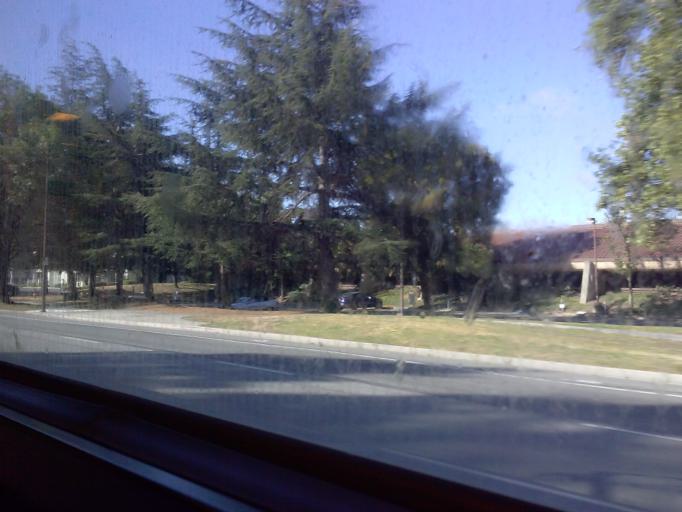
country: US
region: California
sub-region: Santa Clara County
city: Santa Clara
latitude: 37.3909
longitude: -121.9315
